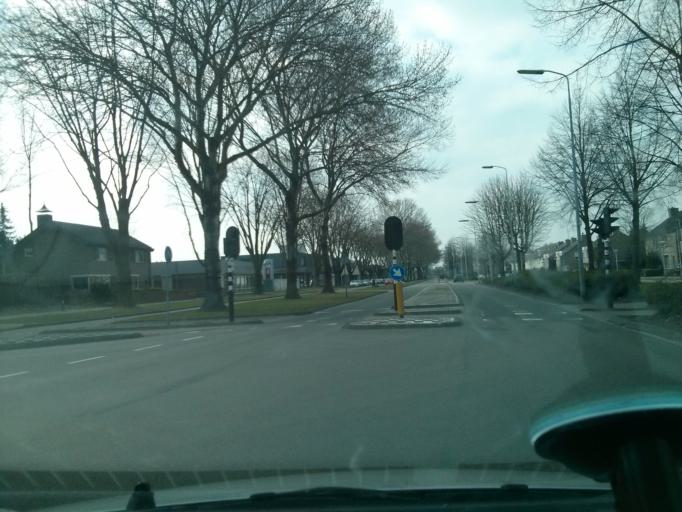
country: NL
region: North Brabant
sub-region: Gemeente Son en Breugel
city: Son
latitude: 51.4838
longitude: 5.4612
